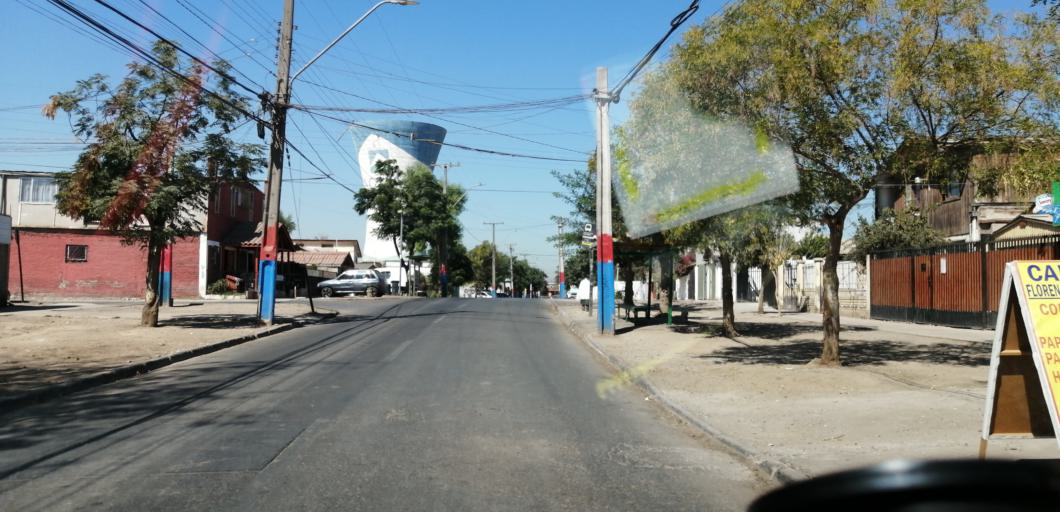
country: CL
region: Santiago Metropolitan
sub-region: Provincia de Santiago
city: Lo Prado
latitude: -33.4403
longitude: -70.7580
